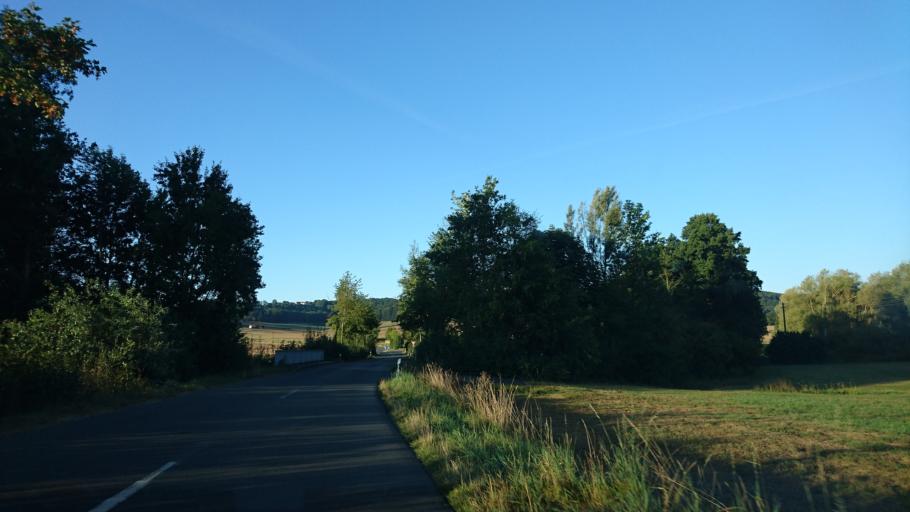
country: DE
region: Bavaria
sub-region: Regierungsbezirk Mittelfranken
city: Thalmassing
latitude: 49.0842
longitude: 11.2504
